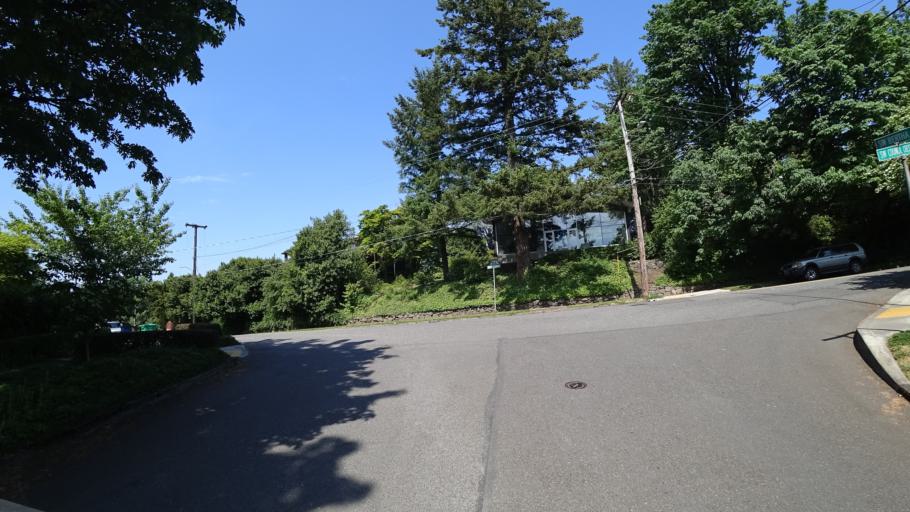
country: US
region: Oregon
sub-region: Multnomah County
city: Portland
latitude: 45.4937
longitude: -122.7020
